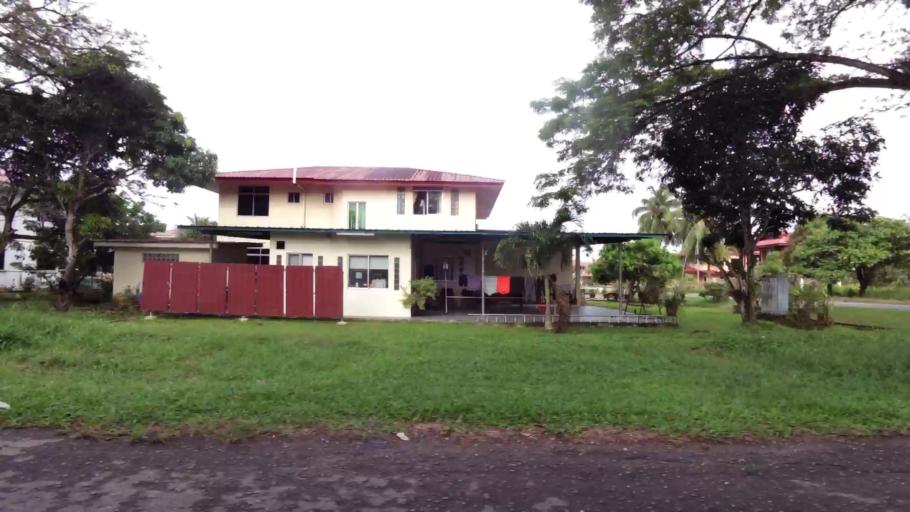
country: BN
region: Belait
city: Seria
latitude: 4.5982
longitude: 114.3274
